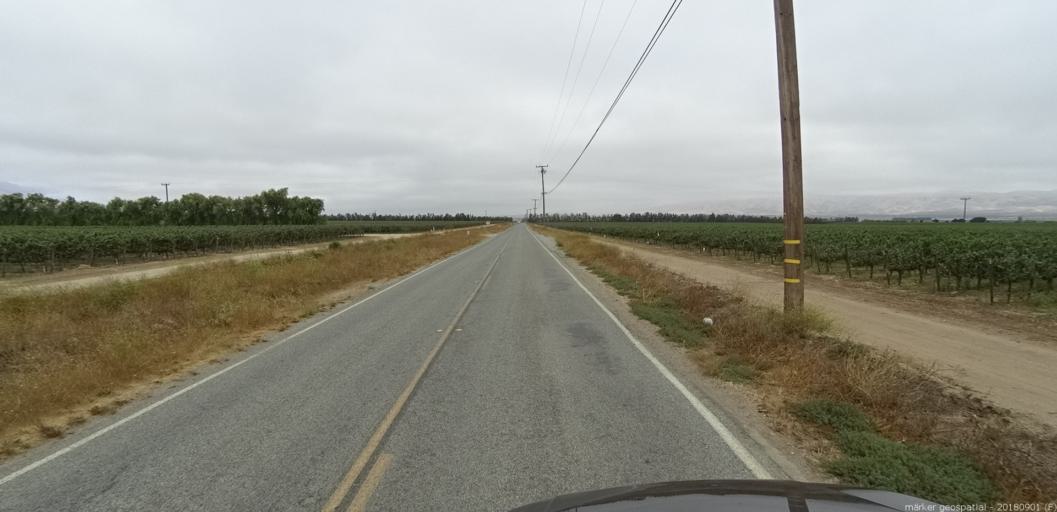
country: US
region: California
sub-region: Monterey County
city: Soledad
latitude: 36.3608
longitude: -121.3208
